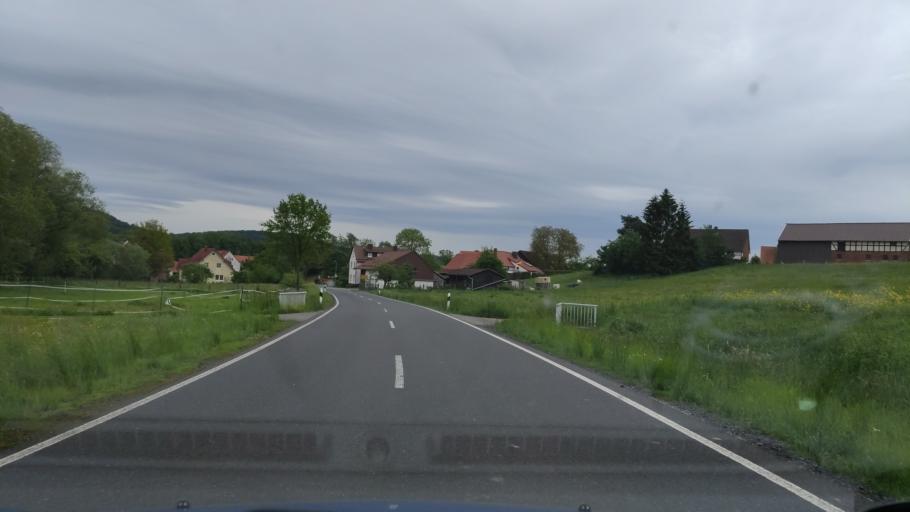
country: DE
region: Lower Saxony
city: Hardegsen
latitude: 51.6920
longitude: 9.7997
